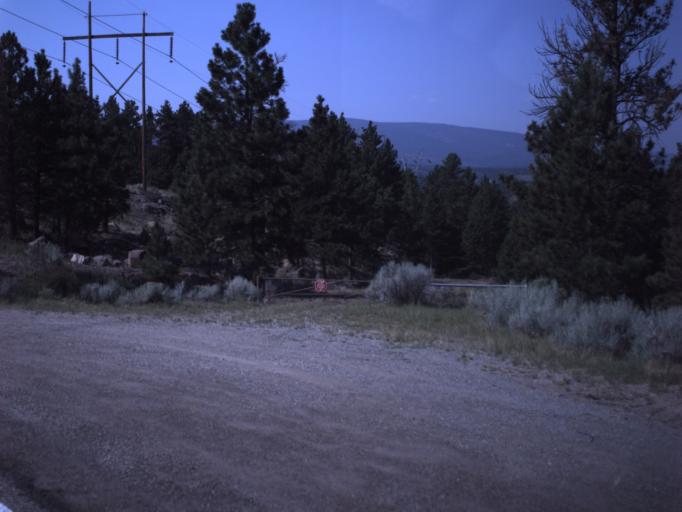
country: US
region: Utah
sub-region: Daggett County
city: Manila
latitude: 40.9173
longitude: -109.4150
